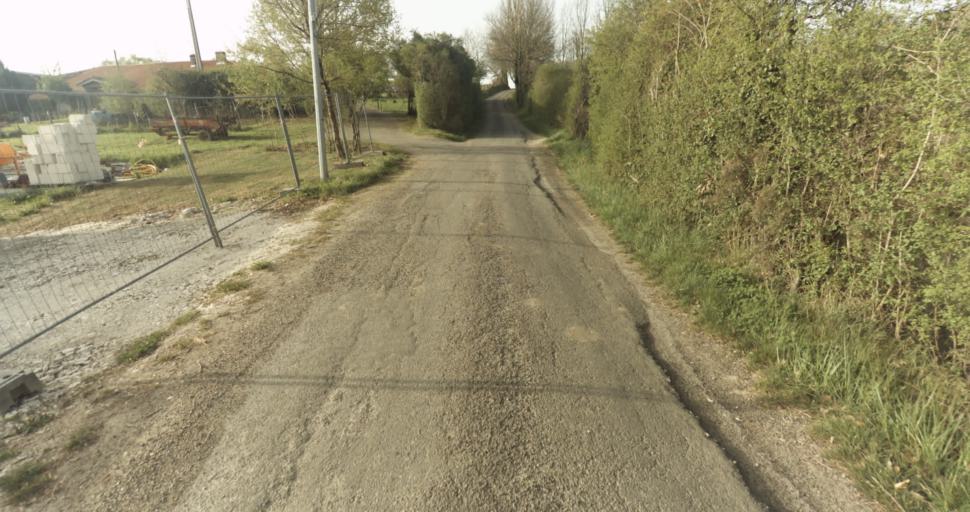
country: FR
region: Midi-Pyrenees
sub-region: Departement du Tarn-et-Garonne
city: Moissac
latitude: 44.1263
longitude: 1.1117
